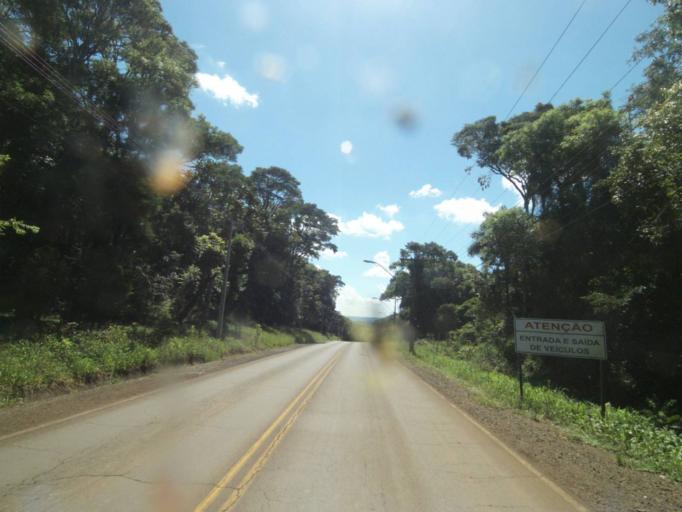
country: BR
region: Parana
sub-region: Chopinzinho
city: Chopinzinho
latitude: -25.7913
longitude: -52.0897
